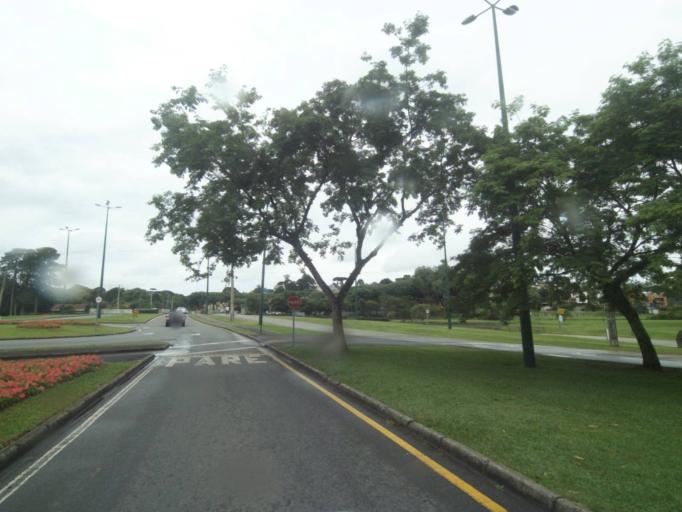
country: BR
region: Parana
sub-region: Curitiba
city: Curitiba
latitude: -25.4234
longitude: -49.3082
